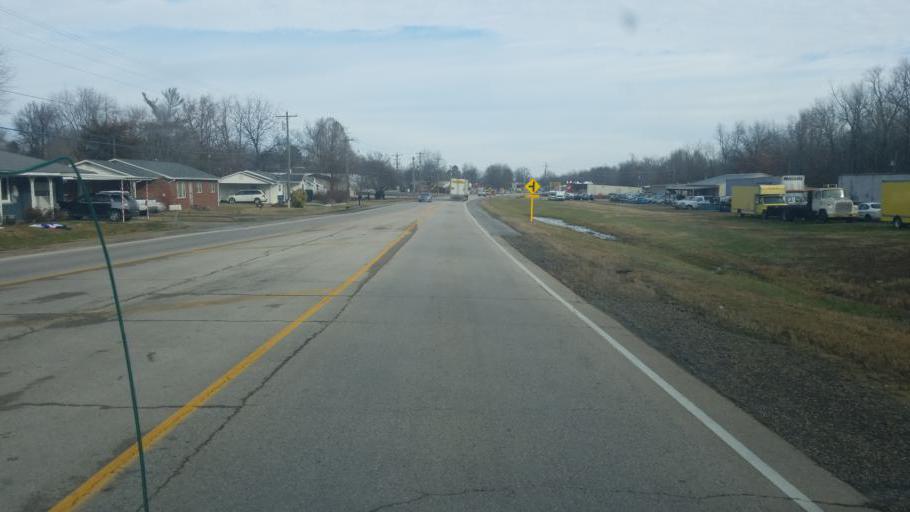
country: US
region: Missouri
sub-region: Stoddard County
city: Bloomfield
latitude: 36.8791
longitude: -89.9269
